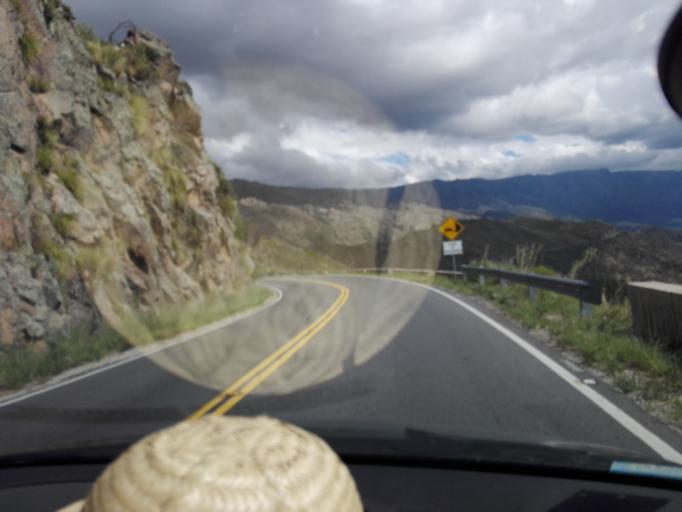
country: AR
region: Cordoba
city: Mina Clavero
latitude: -31.7759
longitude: -64.9139
